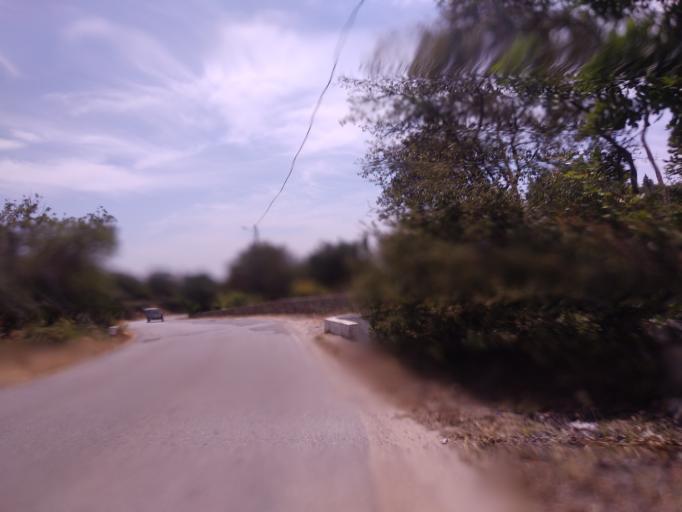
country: PT
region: Faro
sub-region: Faro
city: Santa Barbara de Nexe
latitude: 37.1101
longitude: -7.9473
